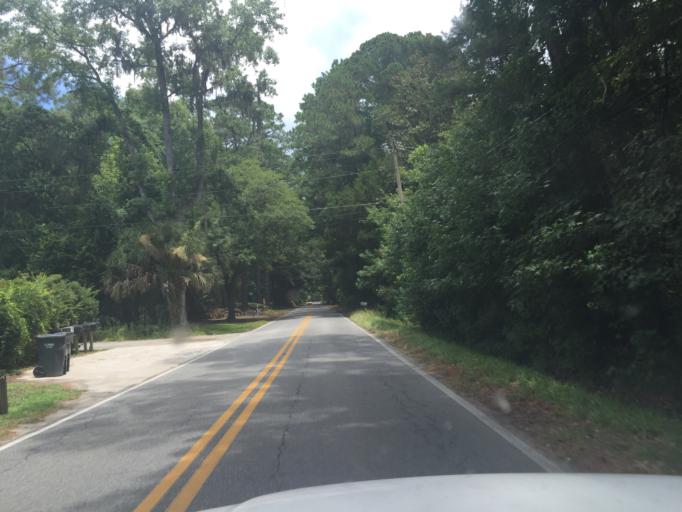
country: US
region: Georgia
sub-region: Chatham County
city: Montgomery
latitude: 31.9533
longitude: -81.1066
